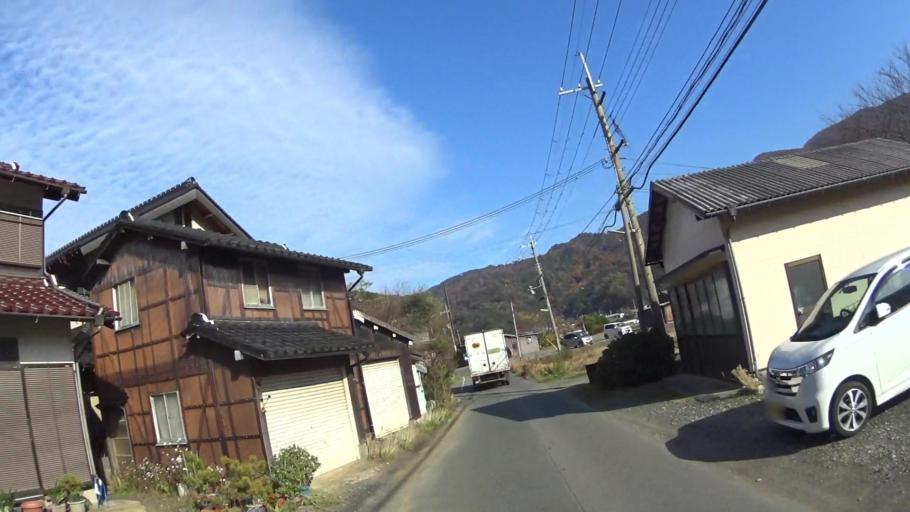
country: JP
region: Kyoto
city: Maizuru
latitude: 35.5579
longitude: 135.3962
